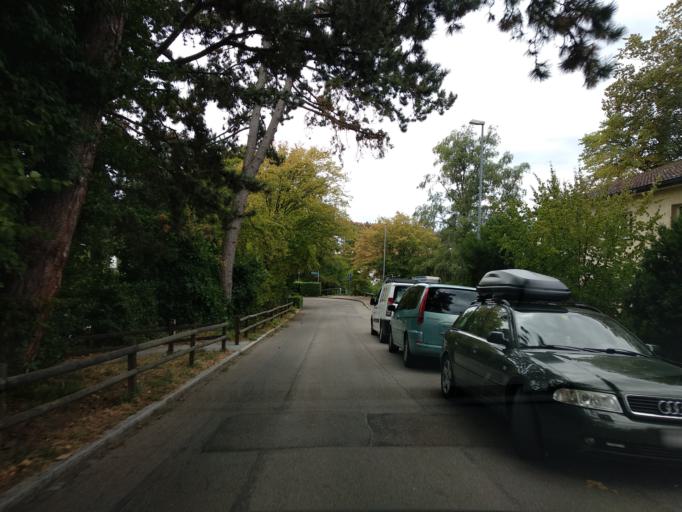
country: CH
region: Schaffhausen
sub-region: Bezirk Schaffhausen
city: Schaffhausen
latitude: 47.7139
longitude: 8.6447
